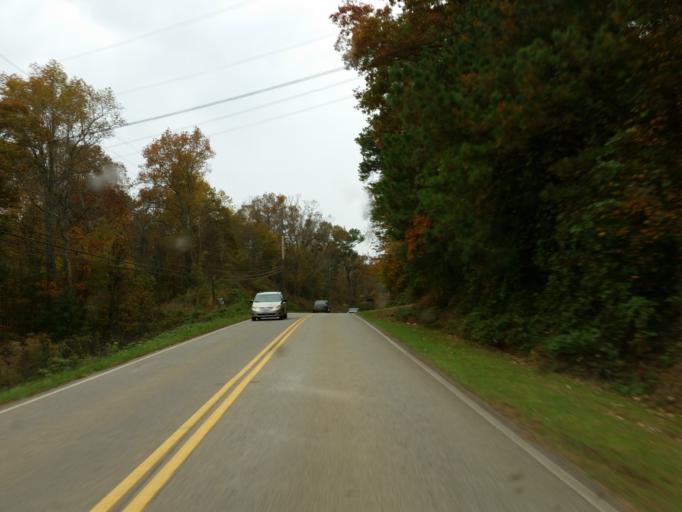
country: US
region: Georgia
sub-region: Pickens County
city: Jasper
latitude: 34.5066
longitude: -84.4406
